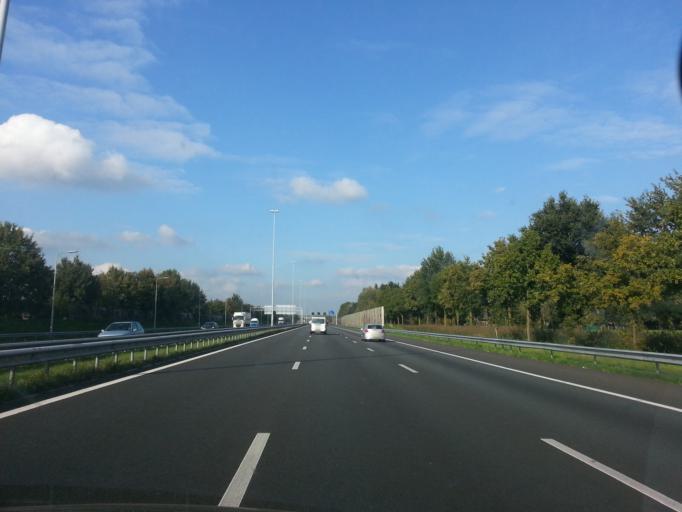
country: NL
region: North Brabant
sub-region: Gemeente Boxtel
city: Boxtel
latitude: 51.5674
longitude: 5.3566
